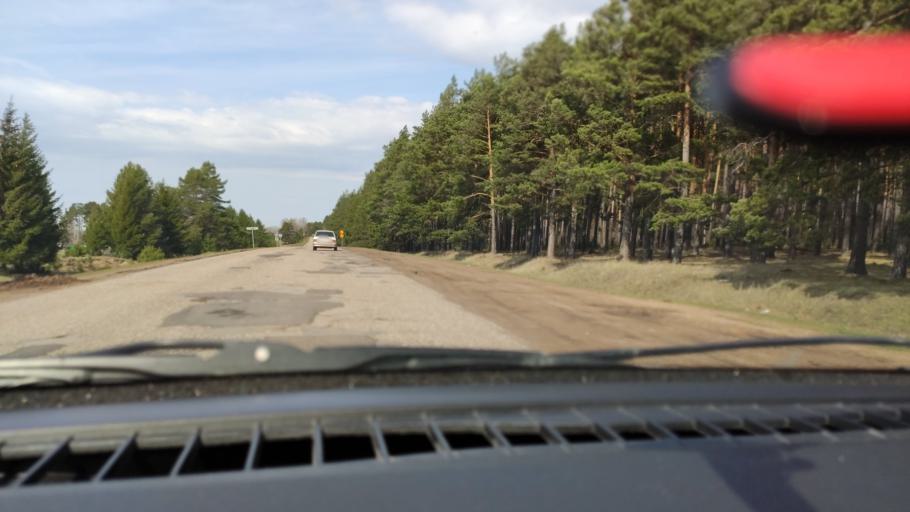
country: RU
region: Bashkortostan
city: Dyurtyuli
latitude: 55.5073
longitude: 54.8928
